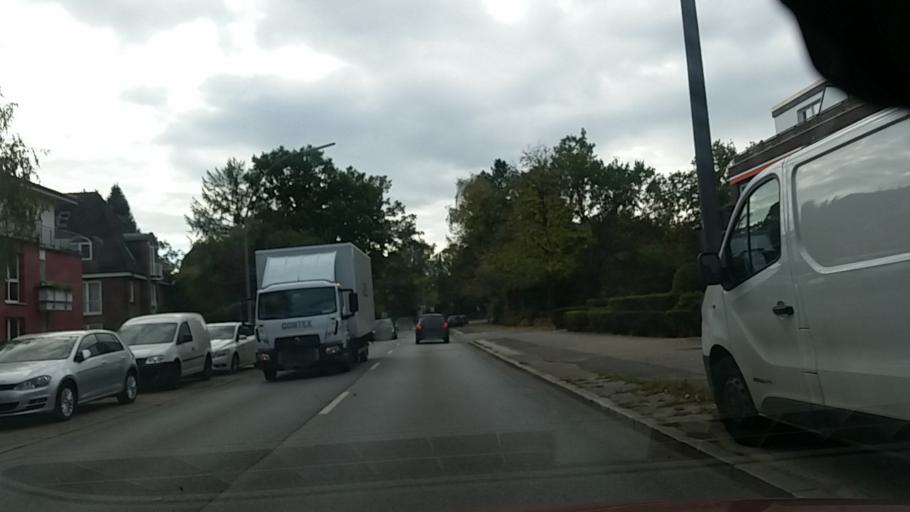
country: DE
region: Hamburg
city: Hummelsbuettel
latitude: 53.6398
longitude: 10.0360
